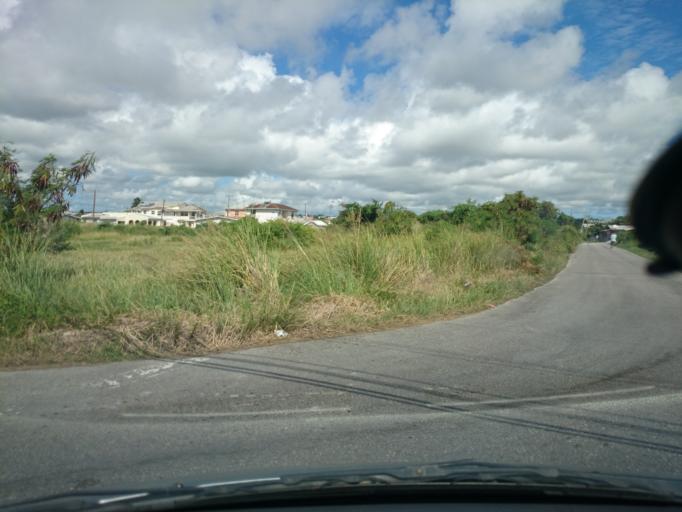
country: BB
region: Christ Church
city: Oistins
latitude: 13.0502
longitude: -59.5262
